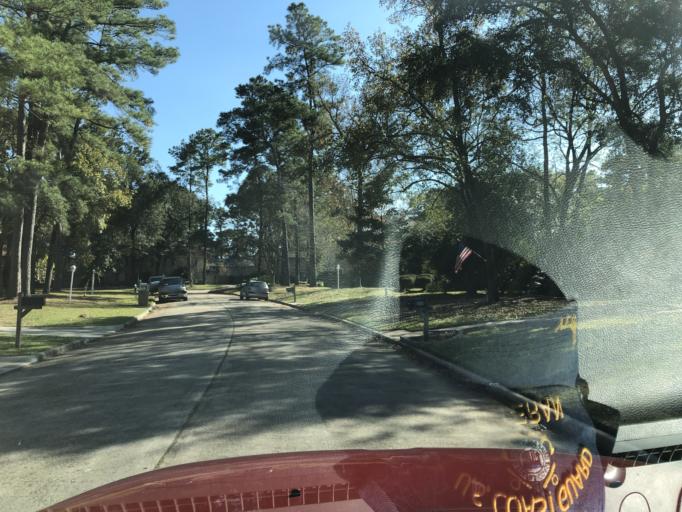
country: US
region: Texas
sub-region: Harris County
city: Tomball
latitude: 30.0292
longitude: -95.5399
